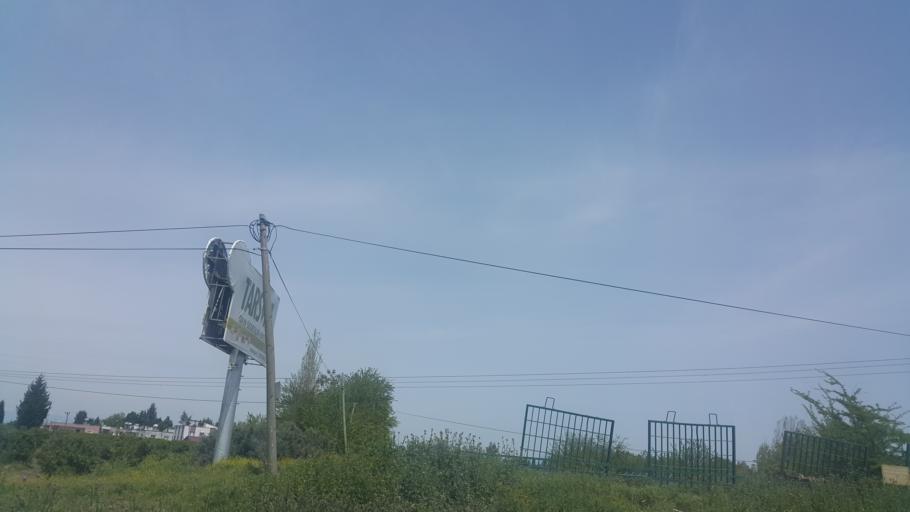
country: TR
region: Osmaniye
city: Toprakkale
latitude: 37.0579
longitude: 36.1200
